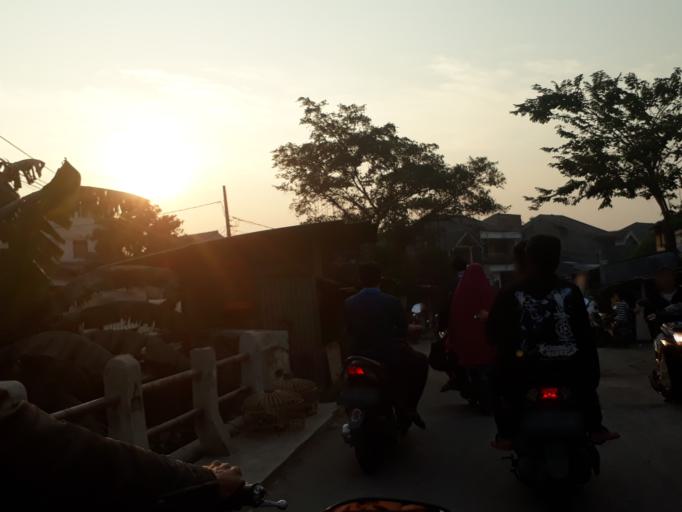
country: ID
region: West Java
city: Bekasi
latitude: -6.2452
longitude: 107.0531
